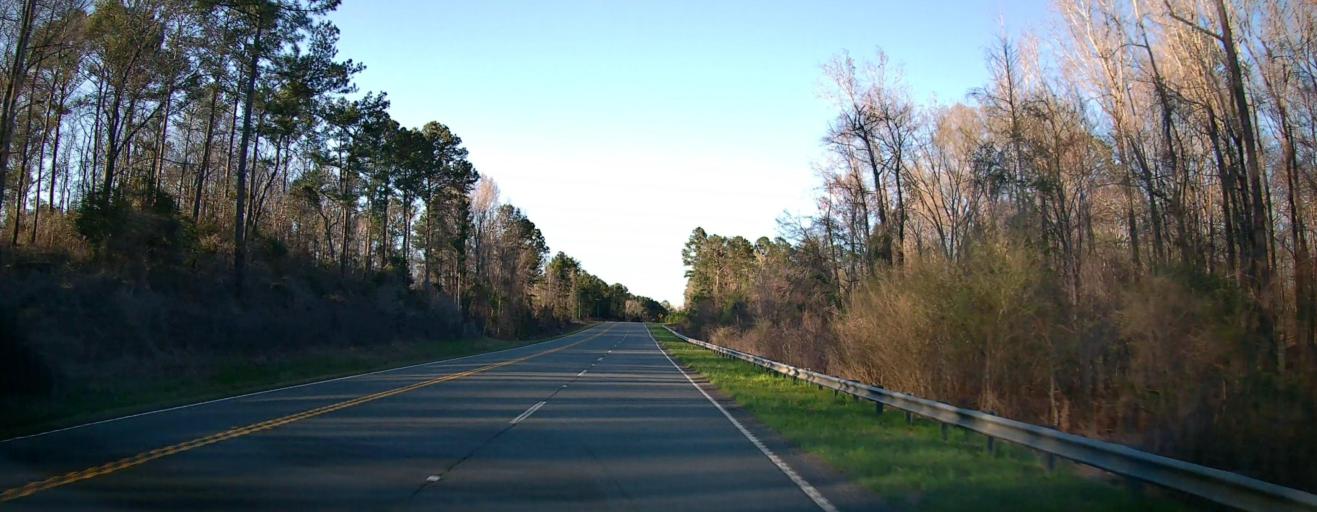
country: US
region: Georgia
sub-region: Talbot County
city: Talbotton
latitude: 32.6024
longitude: -84.5560
